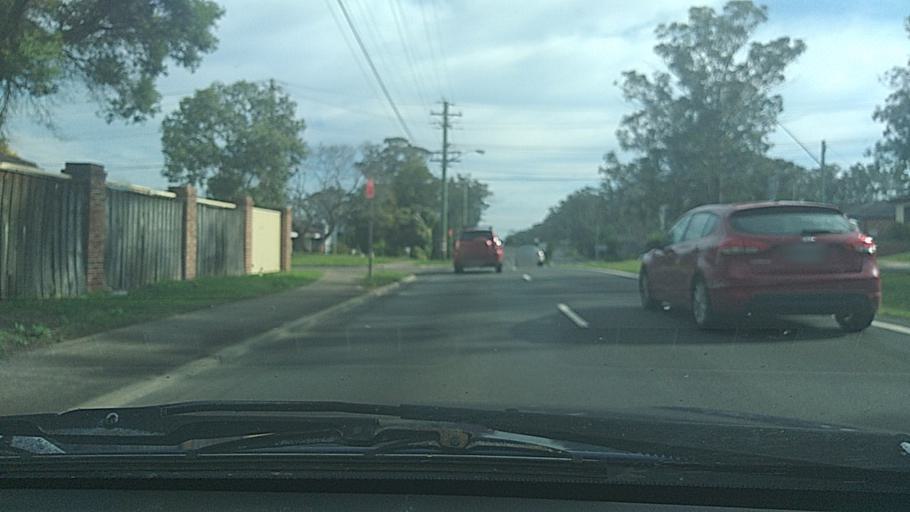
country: AU
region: New South Wales
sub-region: Penrith Municipality
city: Cambridge Park
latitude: -33.7531
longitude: 150.7129
